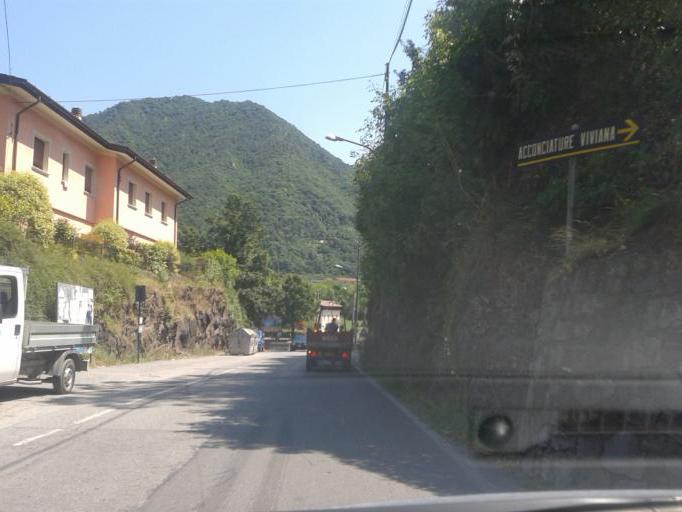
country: IT
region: Lombardy
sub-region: Provincia di Brescia
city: Idro
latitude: 45.7339
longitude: 10.4584
